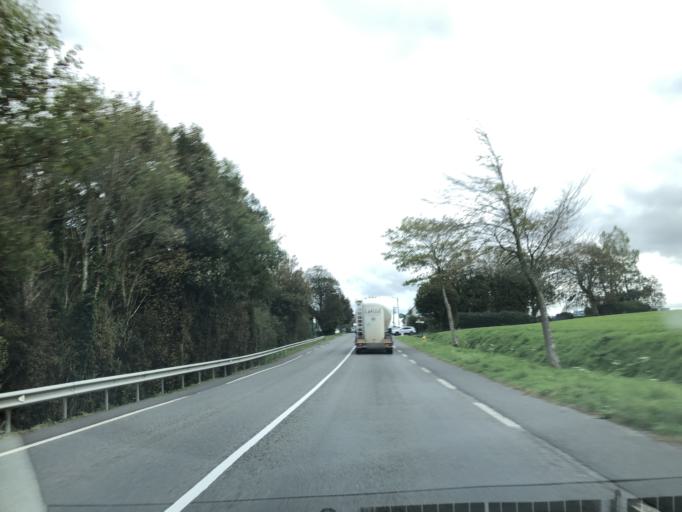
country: FR
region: Nord-Pas-de-Calais
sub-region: Departement du Pas-de-Calais
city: Fruges
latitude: 50.5393
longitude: 2.1062
